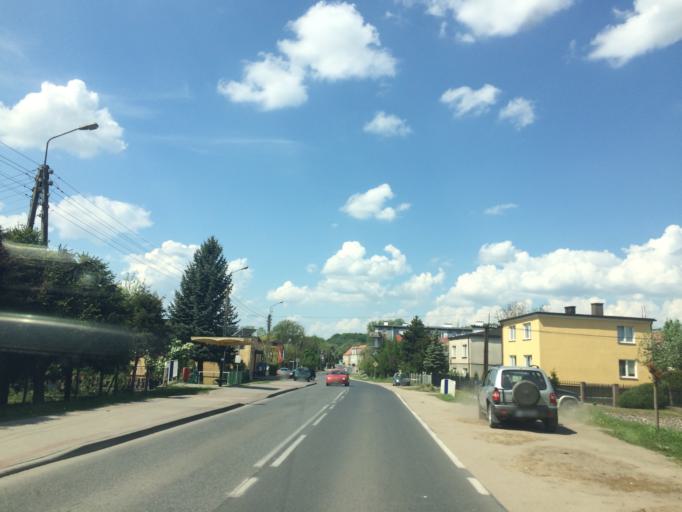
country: PL
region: Warmian-Masurian Voivodeship
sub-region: Powiat nowomiejski
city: Nowe Miasto Lubawskie
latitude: 53.4206
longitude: 19.6013
